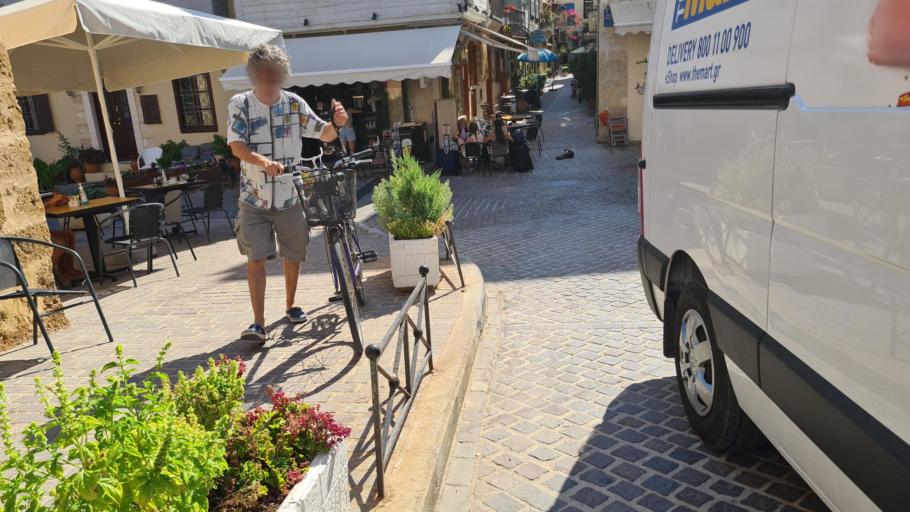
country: GR
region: Crete
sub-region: Nomos Chanias
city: Chania
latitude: 35.5182
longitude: 24.0149
